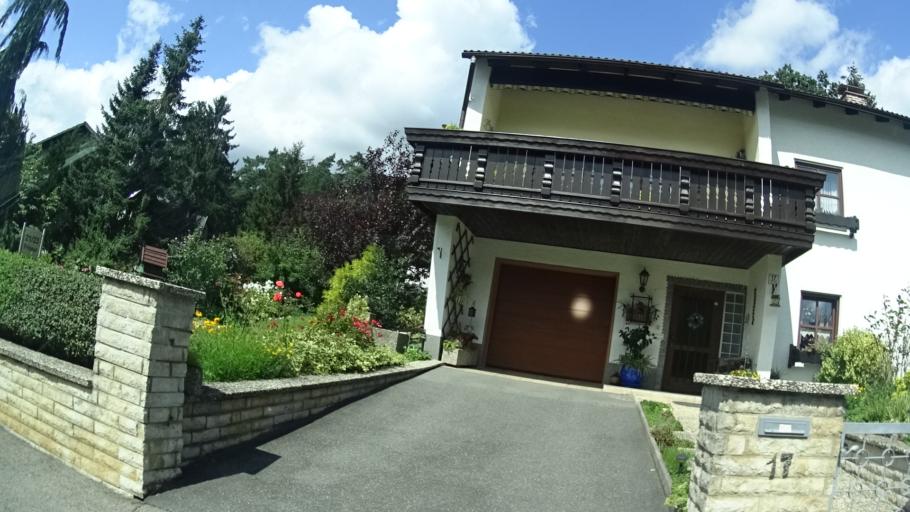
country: DE
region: Bavaria
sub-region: Upper Franconia
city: Rodental
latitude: 50.2340
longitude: 11.0619
